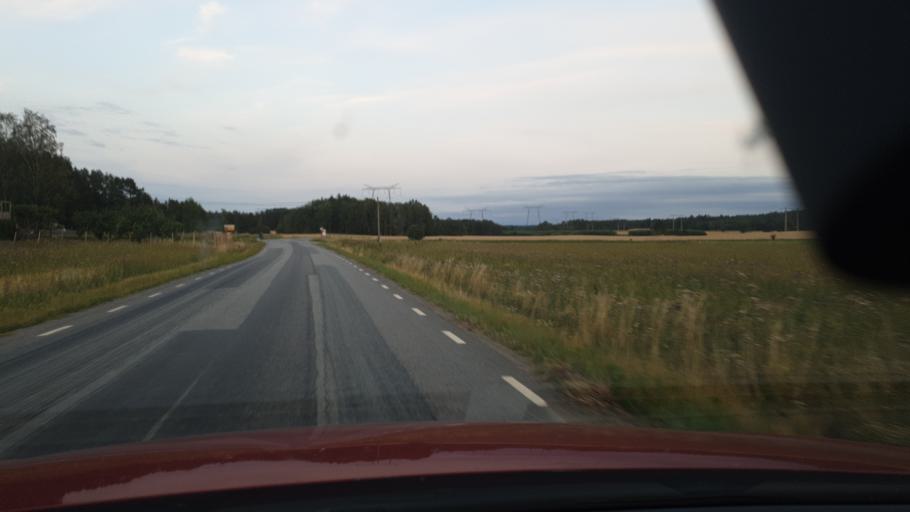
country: SE
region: Uppsala
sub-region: Enkopings Kommun
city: Orsundsbro
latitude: 59.6825
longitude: 17.4032
